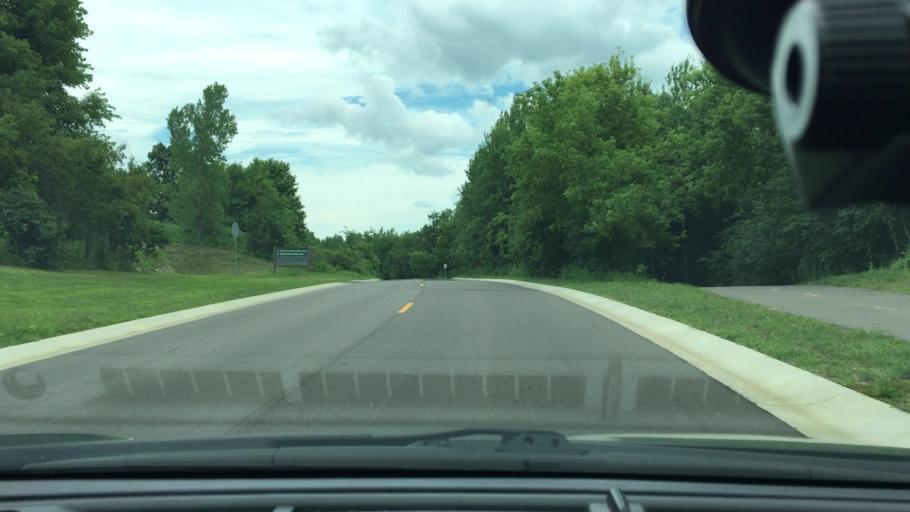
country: US
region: Minnesota
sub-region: Hennepin County
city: Plymouth
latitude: 45.0233
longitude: -93.4341
